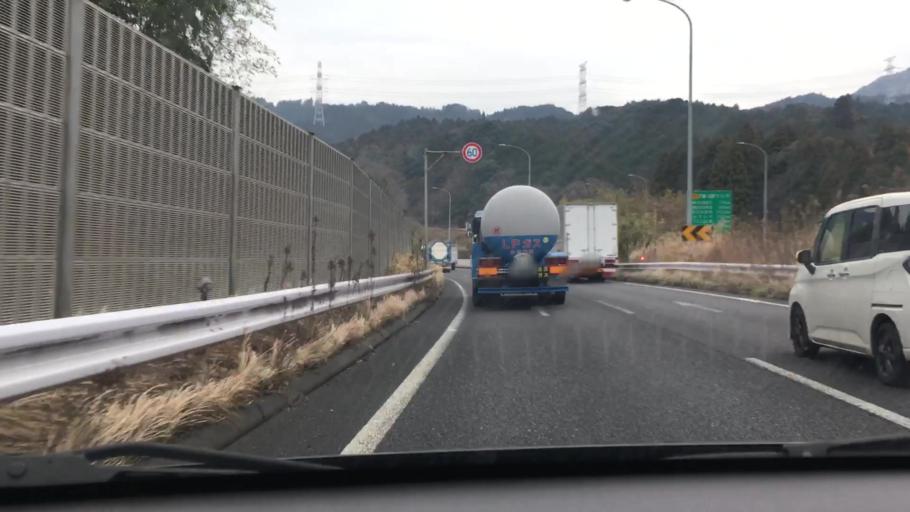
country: JP
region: Mie
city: Kameyama
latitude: 34.8365
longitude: 136.3353
